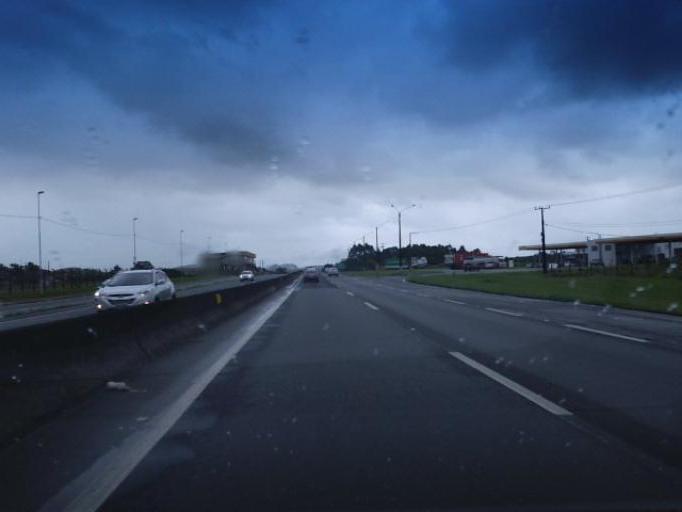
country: BR
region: Santa Catarina
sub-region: Barra Velha
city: Barra Velha
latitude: -26.6301
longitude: -48.7056
